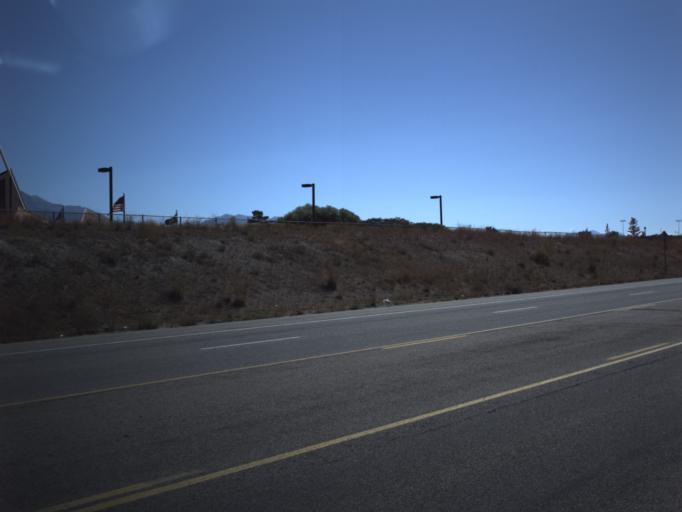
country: US
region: Utah
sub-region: Salt Lake County
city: Bluffdale
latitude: 40.4405
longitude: -111.9326
